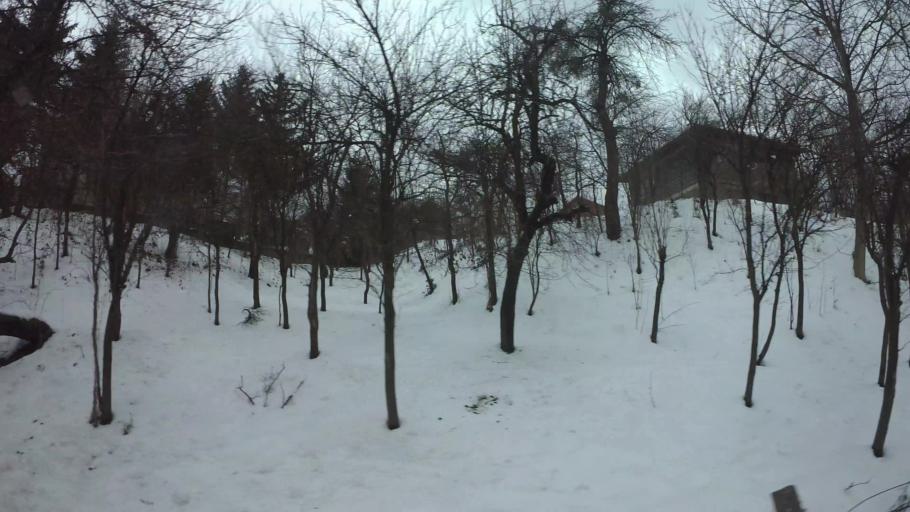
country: BA
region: Federation of Bosnia and Herzegovina
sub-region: Kanton Sarajevo
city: Sarajevo
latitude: 43.8651
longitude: 18.3182
